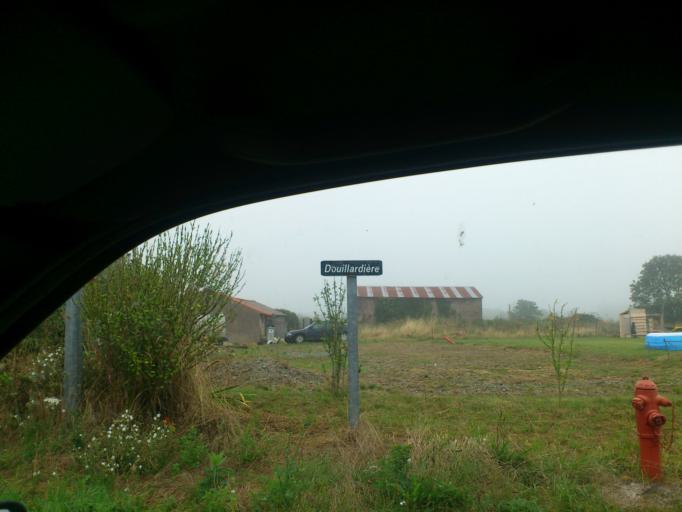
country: FR
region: Pays de la Loire
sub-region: Departement de la Vendee
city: Saint-Hilaire-de-Loulay
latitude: 47.0224
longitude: -1.3142
